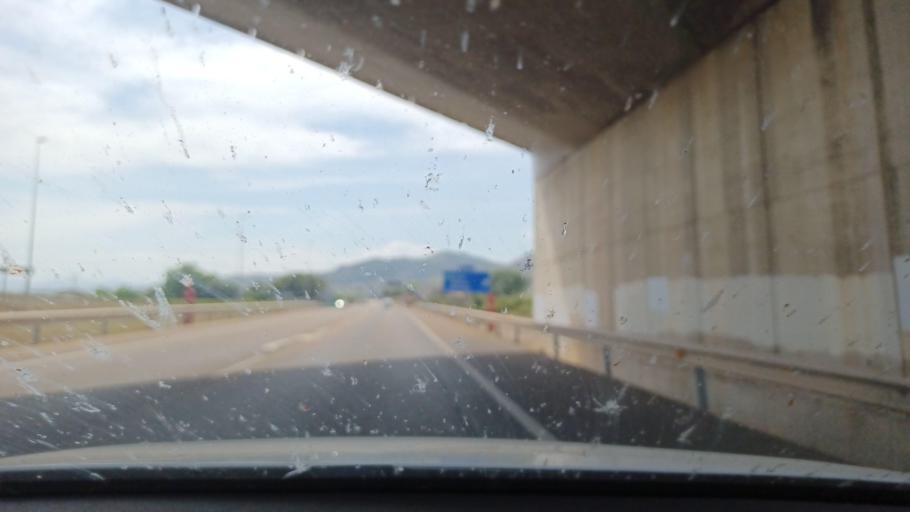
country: ES
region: Valencia
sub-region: Provincia de Castello
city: Castello de la Plana
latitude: 40.0248
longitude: -0.0179
